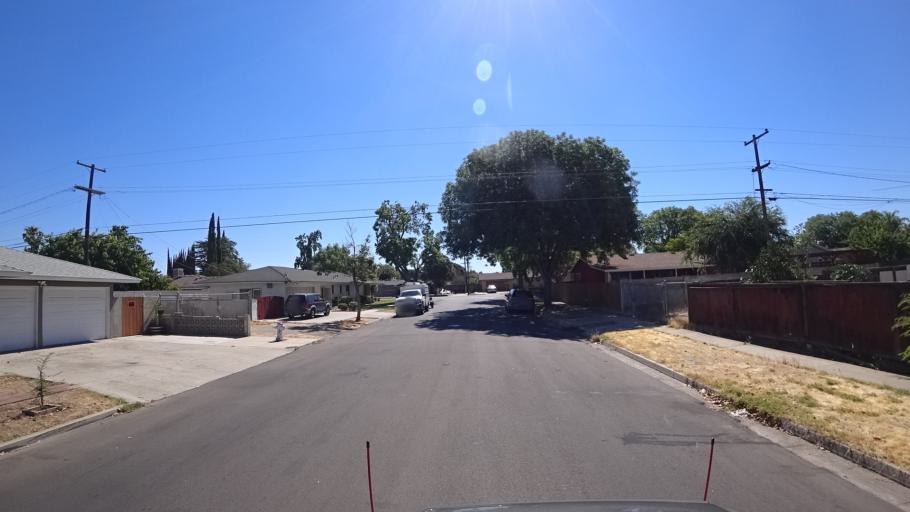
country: US
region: California
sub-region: Fresno County
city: Fresno
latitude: 36.7820
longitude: -119.8351
